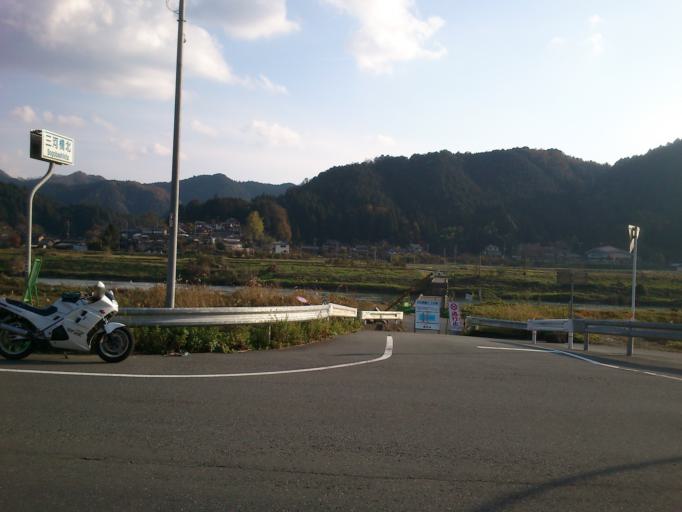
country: JP
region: Kyoto
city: Miyazu
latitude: 35.4111
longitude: 135.1937
